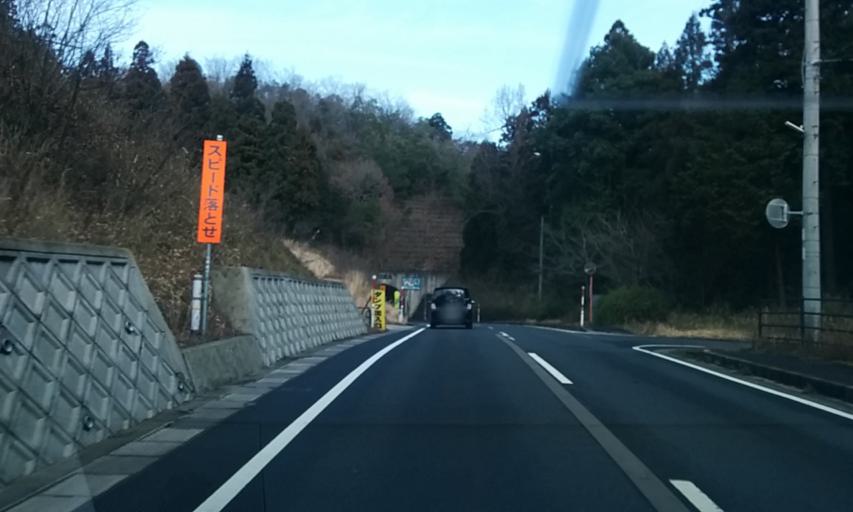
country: JP
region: Kyoto
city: Miyazu
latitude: 35.5810
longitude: 135.1179
